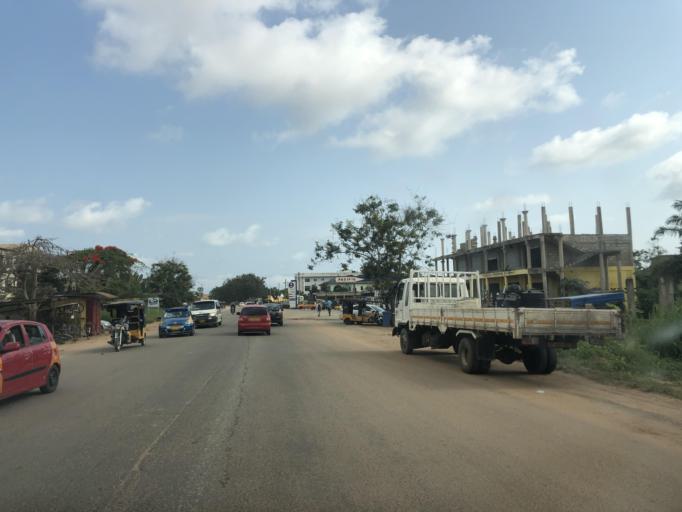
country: GH
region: Central
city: Cape Coast
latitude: 5.1393
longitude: -1.2813
